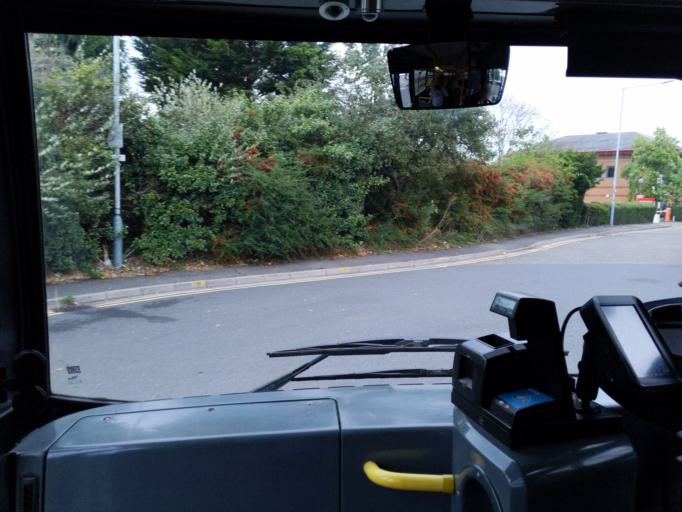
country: GB
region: England
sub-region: Greater London
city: West Drayton
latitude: 51.4819
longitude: -0.4455
